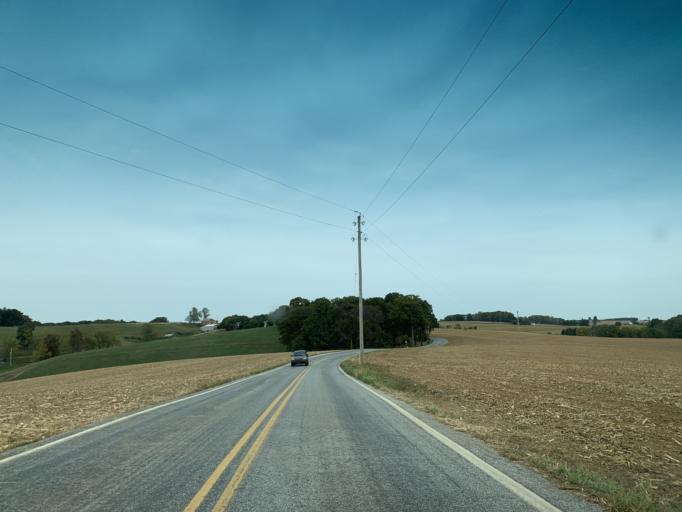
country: US
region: Pennsylvania
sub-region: York County
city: Windsor
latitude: 39.8614
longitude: -76.5138
